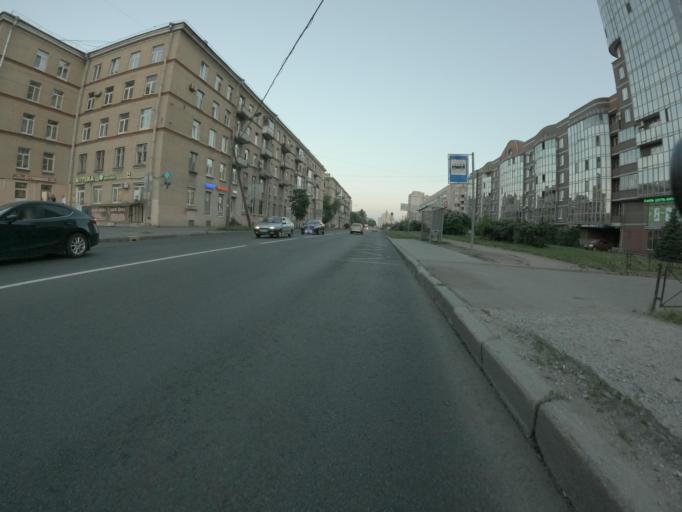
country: RU
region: St.-Petersburg
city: Kupchino
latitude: 59.8517
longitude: 30.3147
